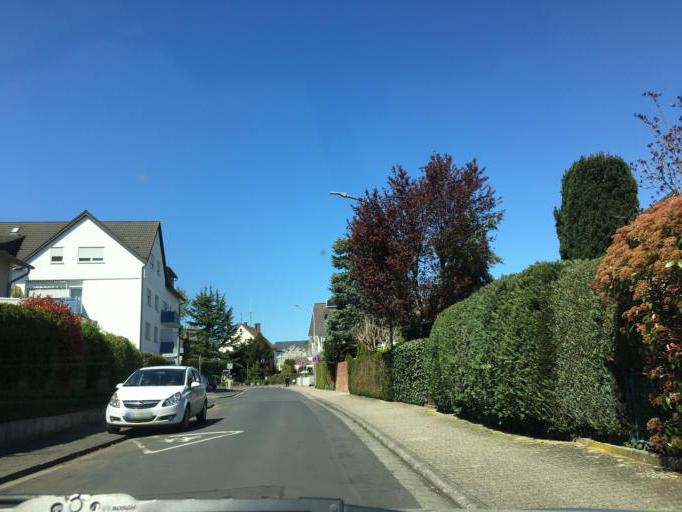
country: DE
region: Hesse
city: Obertshausen
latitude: 50.0749
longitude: 8.8627
